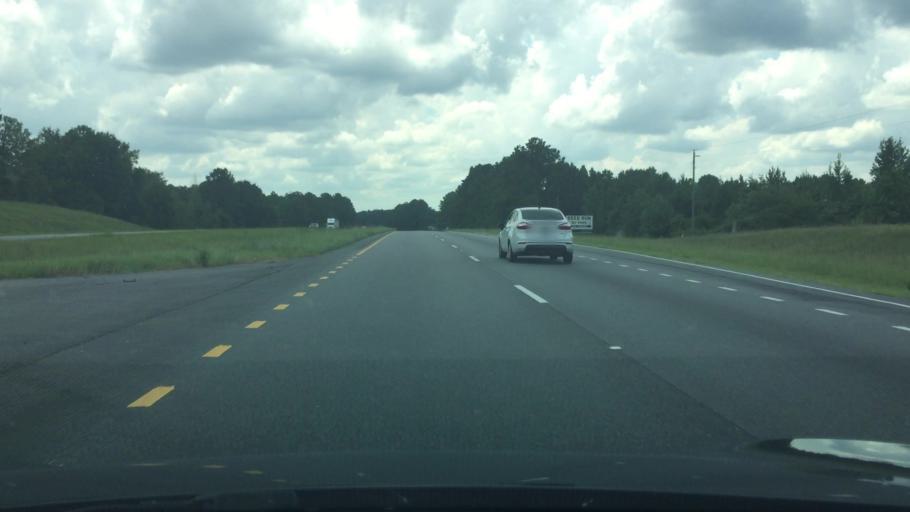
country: US
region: Alabama
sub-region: Pike County
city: Troy
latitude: 31.9010
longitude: -86.0109
